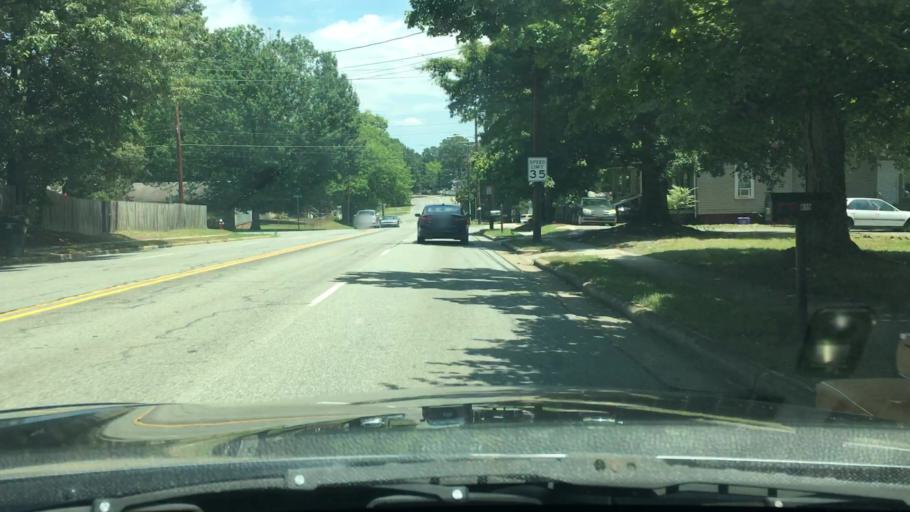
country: US
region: North Carolina
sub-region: Alamance County
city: Burlington
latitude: 36.0922
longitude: -79.4261
